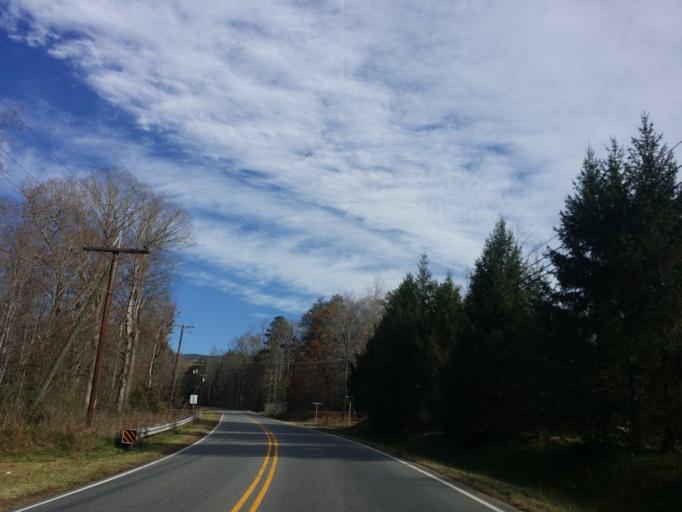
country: US
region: North Carolina
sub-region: McDowell County
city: West Marion
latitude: 35.6471
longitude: -82.1565
